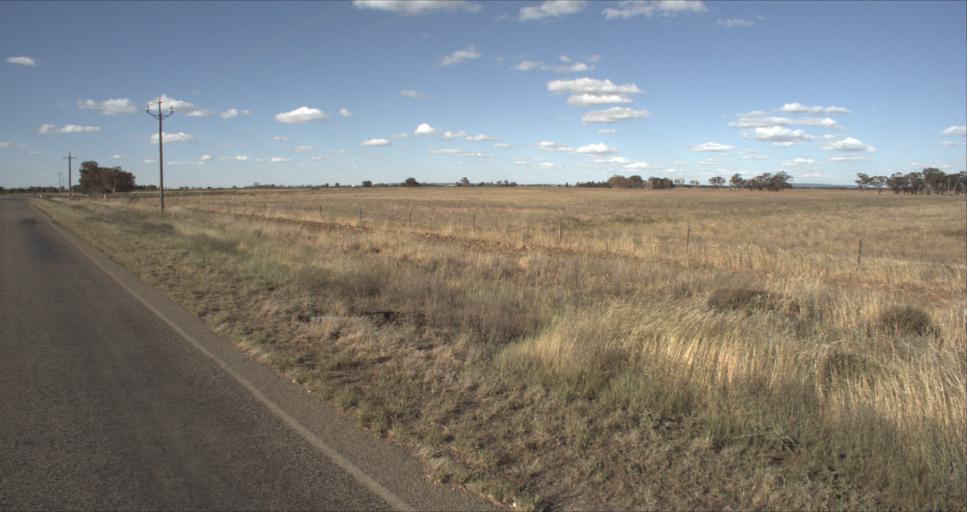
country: AU
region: New South Wales
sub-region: Leeton
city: Leeton
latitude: -34.5393
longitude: 146.2801
